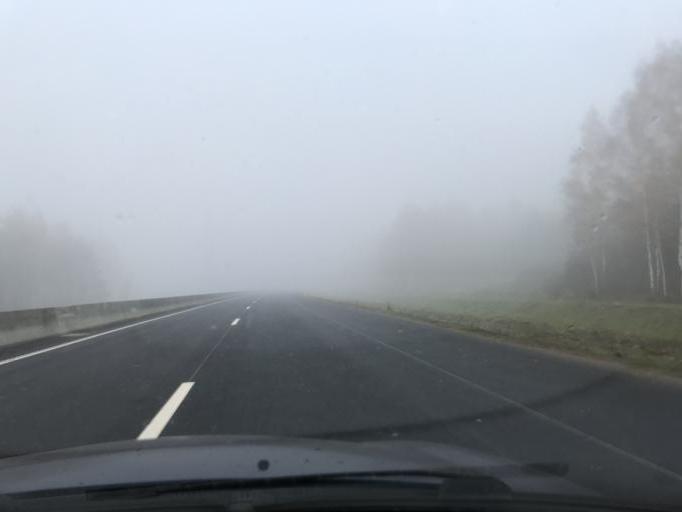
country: BY
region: Minsk
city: Valozhyn
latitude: 54.0404
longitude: 26.5877
